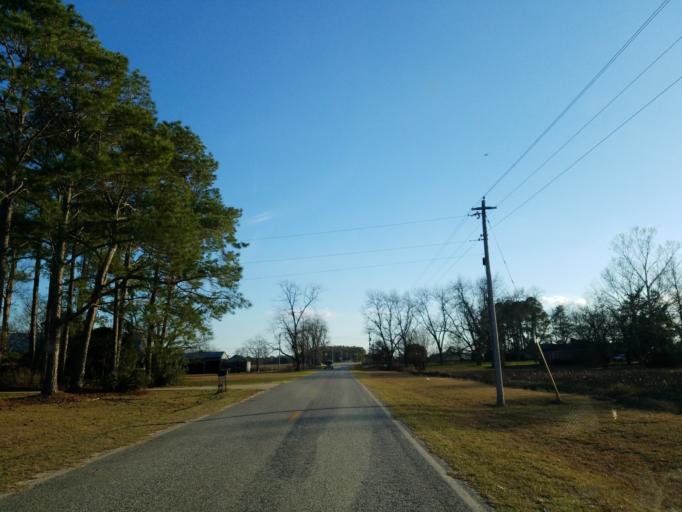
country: US
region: Georgia
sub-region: Crisp County
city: Cordele
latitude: 31.8660
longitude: -83.7967
